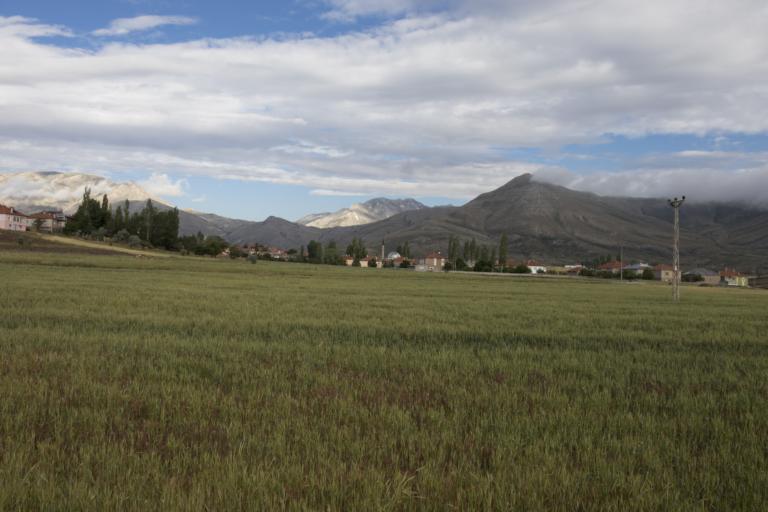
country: TR
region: Kayseri
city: Toklar
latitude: 38.4096
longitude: 36.0762
